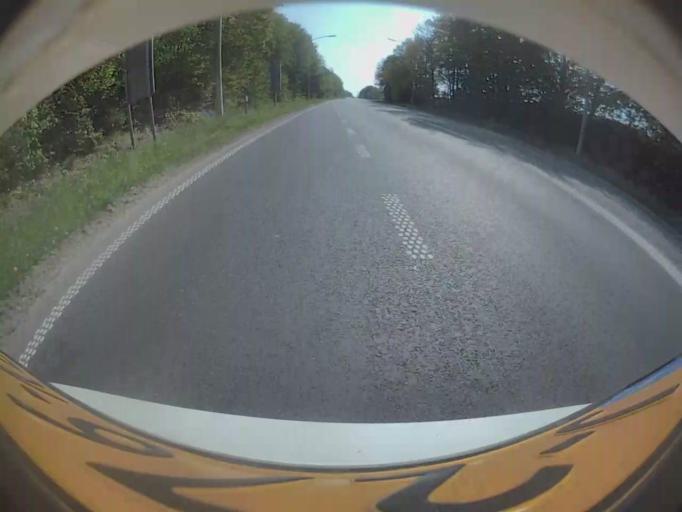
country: BE
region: Wallonia
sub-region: Province de Namur
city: Hamois
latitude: 50.3168
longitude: 5.1286
